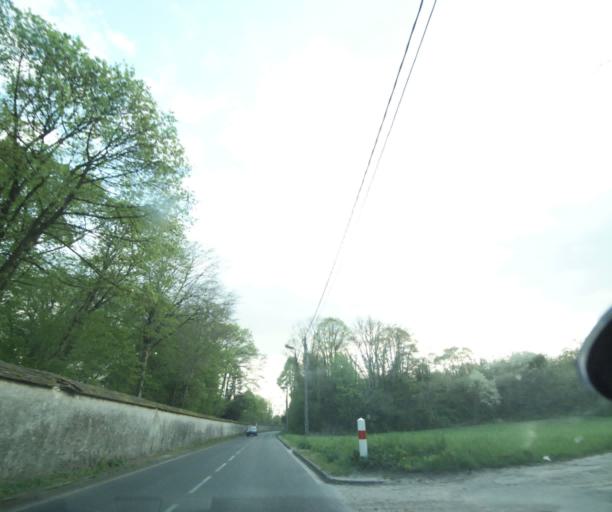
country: FR
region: Ile-de-France
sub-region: Departement de Seine-et-Marne
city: Montigny-sur-Loing
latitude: 48.3380
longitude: 2.7621
